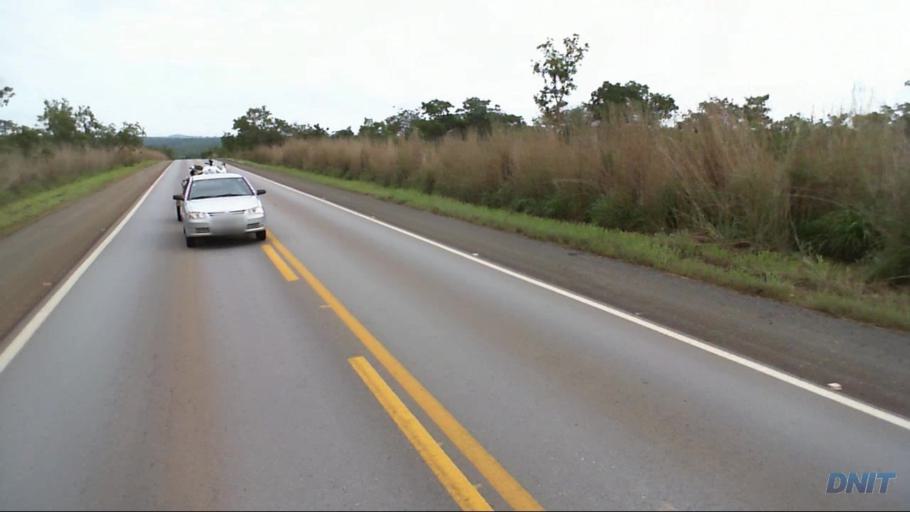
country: BR
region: Goias
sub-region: Uruacu
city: Uruacu
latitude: -14.7599
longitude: -49.0652
